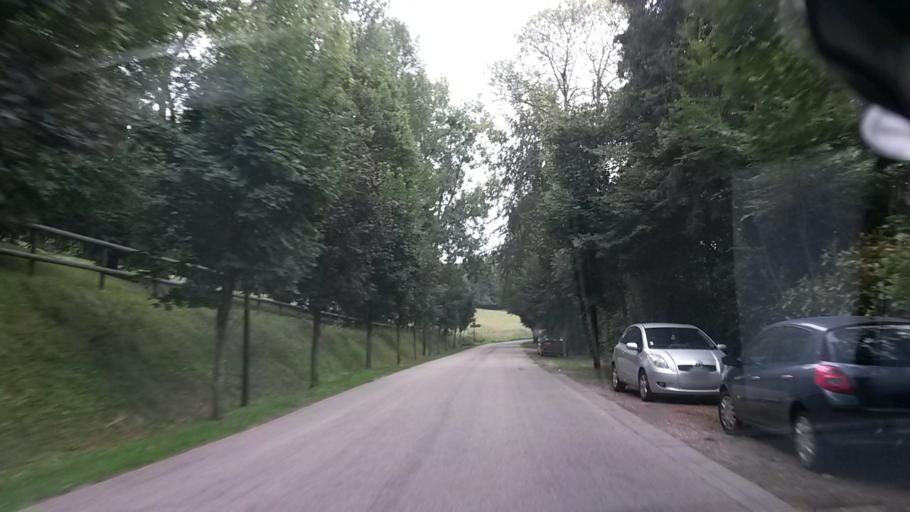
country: FR
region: Haute-Normandie
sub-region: Departement de la Seine-Maritime
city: La Feuillie
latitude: 49.3976
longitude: 1.4768
